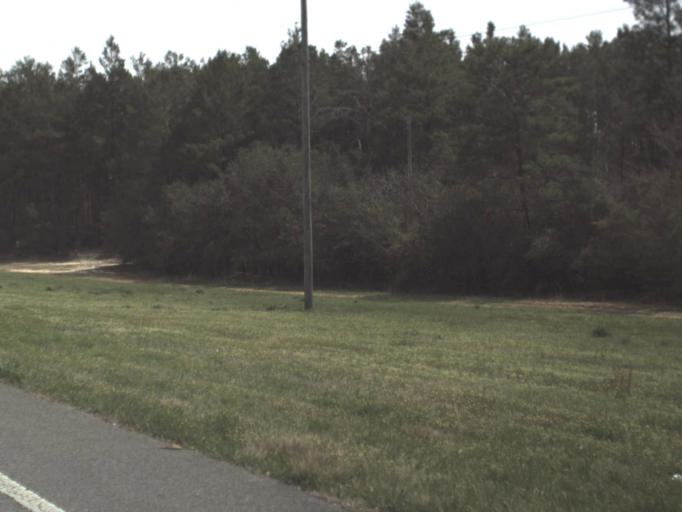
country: US
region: Alabama
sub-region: Geneva County
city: Geneva
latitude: 30.9495
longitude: -85.8372
